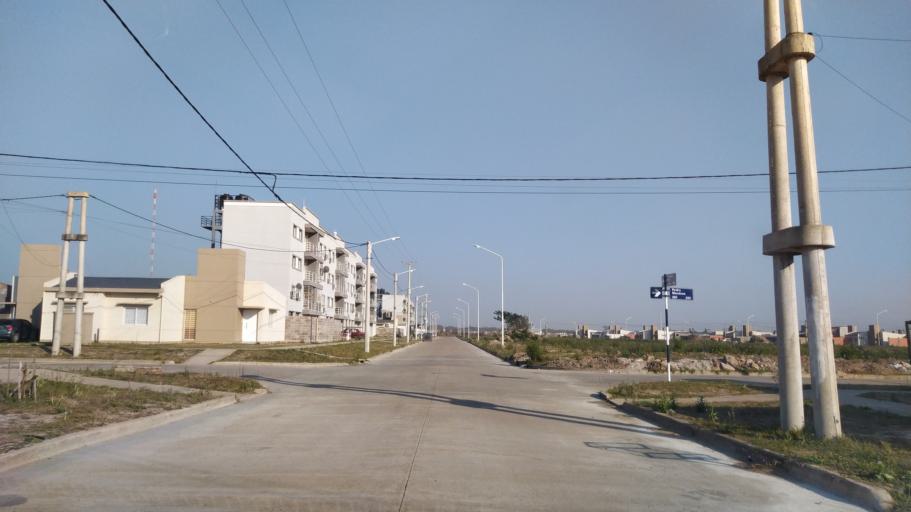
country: AR
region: Corrientes
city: Corrientes
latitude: -27.5277
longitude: -58.8048
